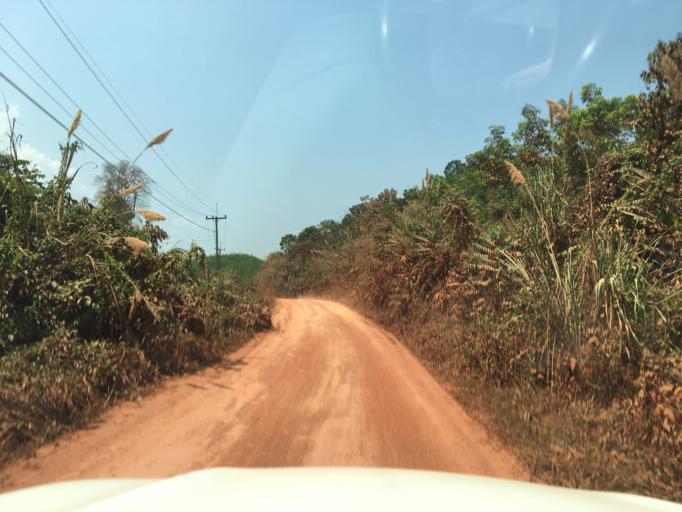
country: LA
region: Bolikhamxai
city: Bolikhan
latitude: 18.7299
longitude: 103.6345
